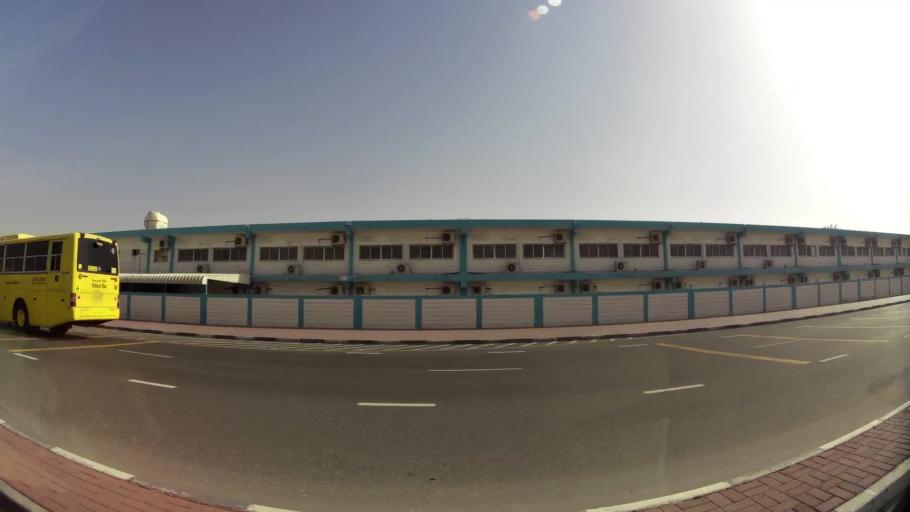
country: AE
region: Ash Shariqah
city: Sharjah
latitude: 25.2393
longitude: 55.3469
